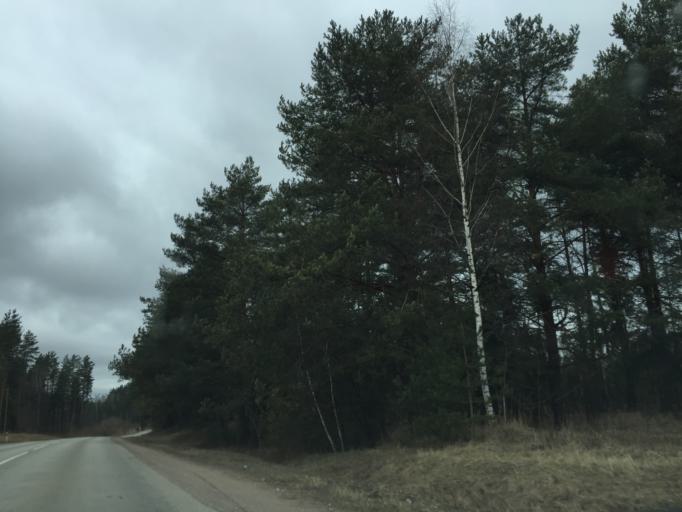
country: LV
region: Ilukste
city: Ilukste
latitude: 55.9179
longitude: 26.3303
